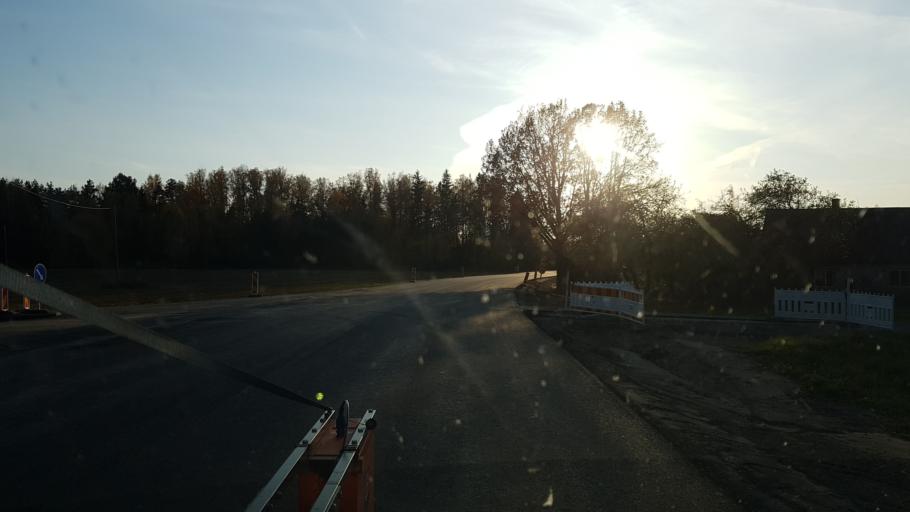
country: EE
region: Polvamaa
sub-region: Polva linn
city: Polva
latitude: 57.9446
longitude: 27.2130
